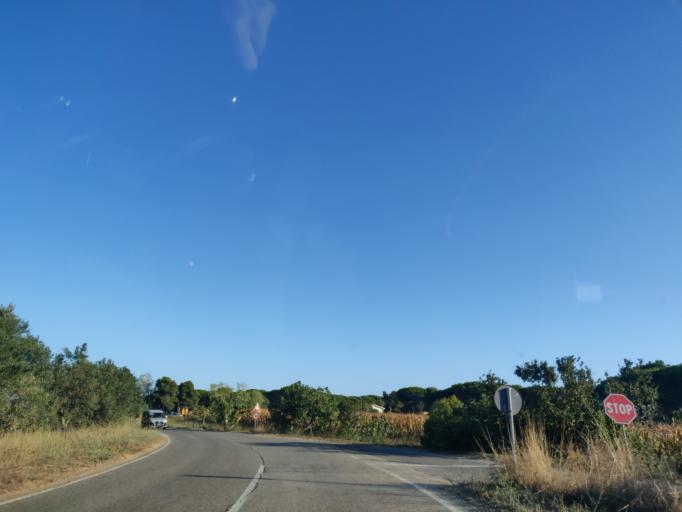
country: IT
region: Latium
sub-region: Provincia di Viterbo
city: Montalto di Castro
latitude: 42.2970
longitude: 11.6483
